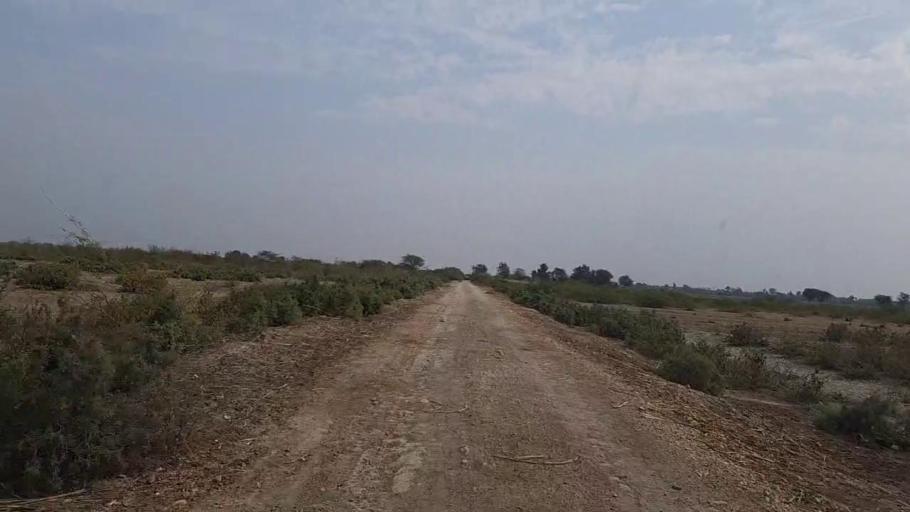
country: PK
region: Sindh
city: Mirwah Gorchani
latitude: 25.3909
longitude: 69.0583
